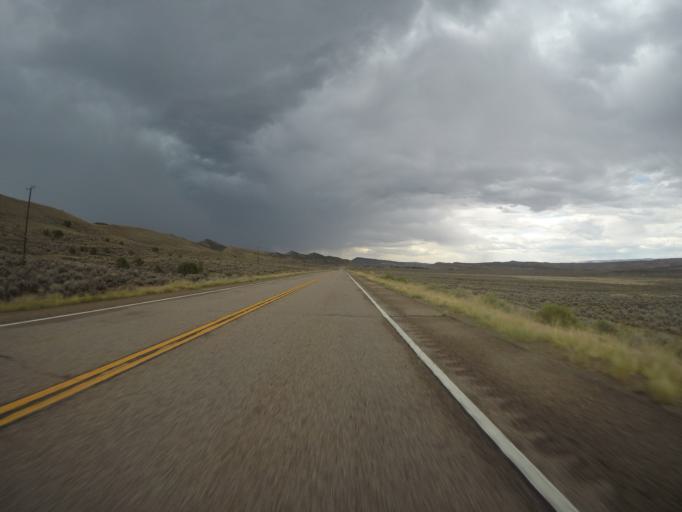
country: US
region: Colorado
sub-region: Rio Blanco County
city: Rangely
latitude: 40.2445
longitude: -108.8864
